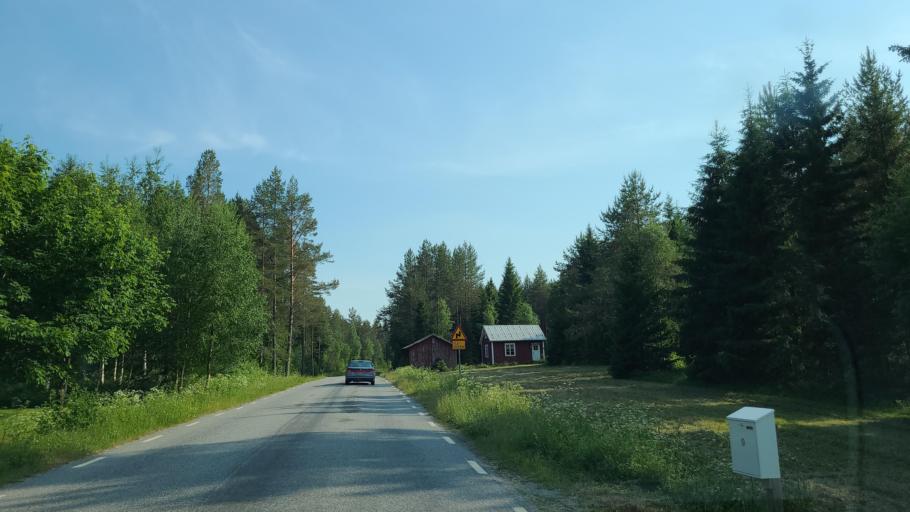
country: SE
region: Vaesterbotten
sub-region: Skelleftea Kommun
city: Burea
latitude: 64.3569
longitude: 21.3378
